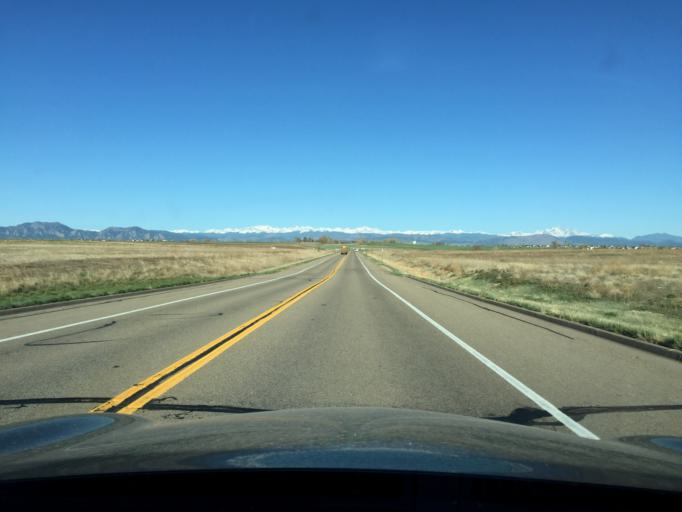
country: US
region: Colorado
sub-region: Boulder County
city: Erie
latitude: 40.0212
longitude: -105.0475
